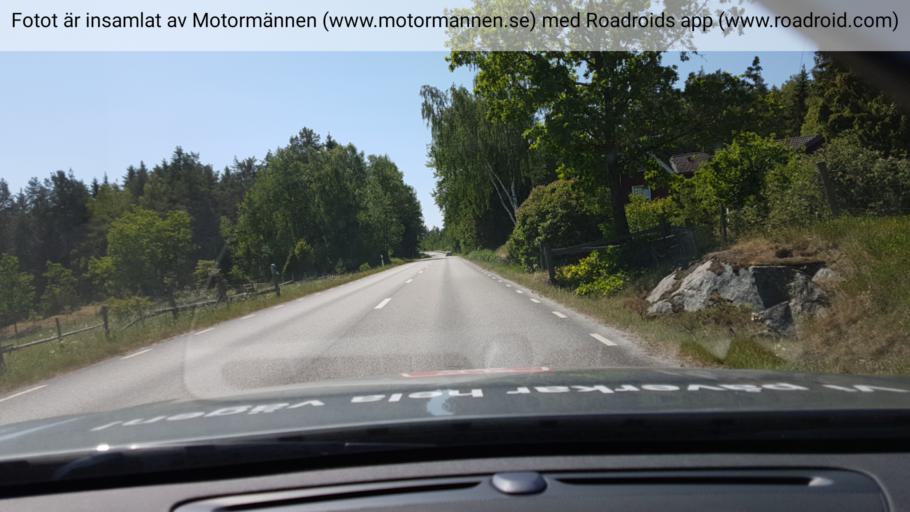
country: SE
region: Stockholm
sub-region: Norrtalje Kommun
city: Rimbo
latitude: 59.6723
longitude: 18.3545
